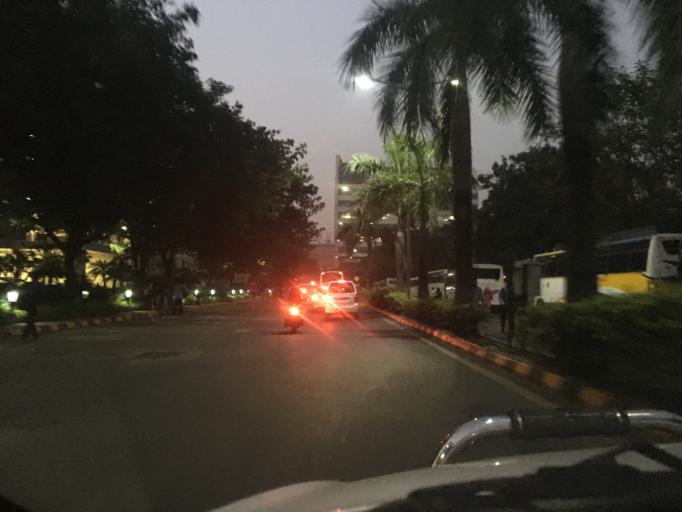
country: IN
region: Maharashtra
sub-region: Thane
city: Airoli
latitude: 19.1610
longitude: 73.0019
